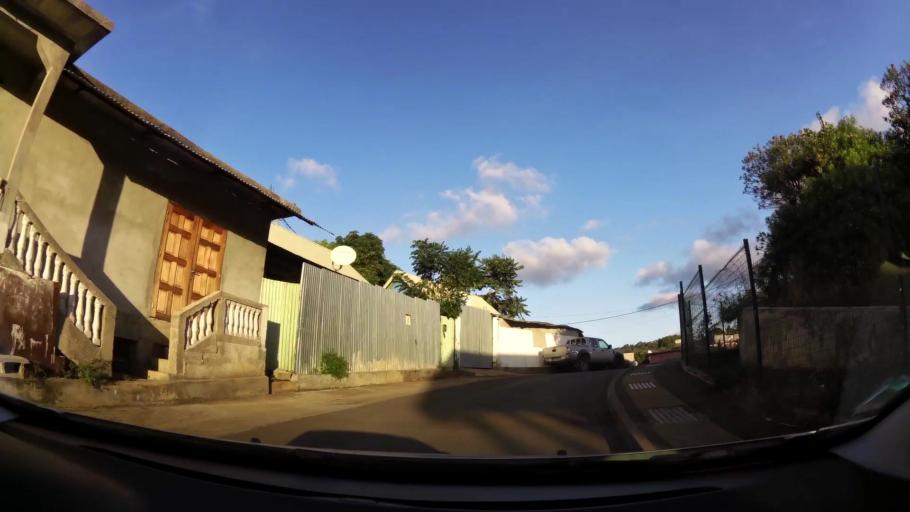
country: YT
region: Dembeni
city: Dembeni
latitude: -12.8453
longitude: 45.1886
